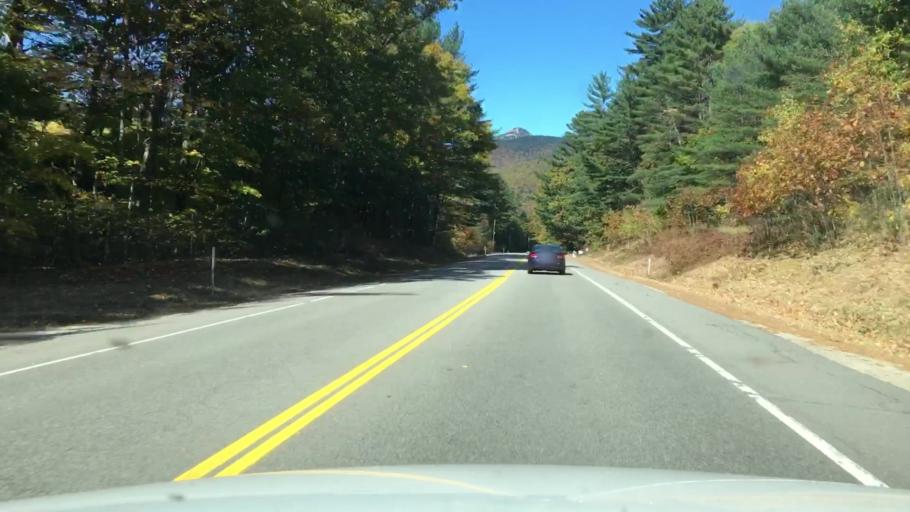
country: US
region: New Hampshire
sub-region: Carroll County
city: Tamworth
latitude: 43.9092
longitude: -71.2343
